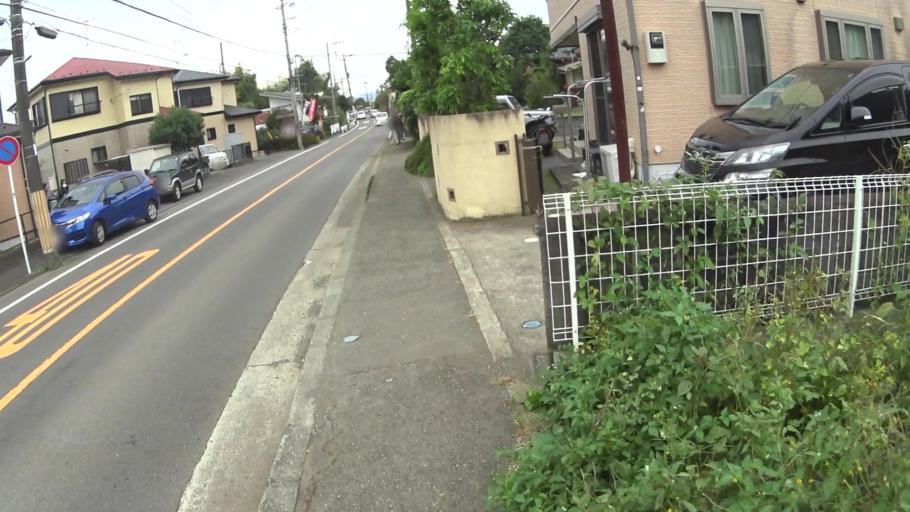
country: JP
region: Kanagawa
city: Hadano
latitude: 35.3953
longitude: 139.2233
